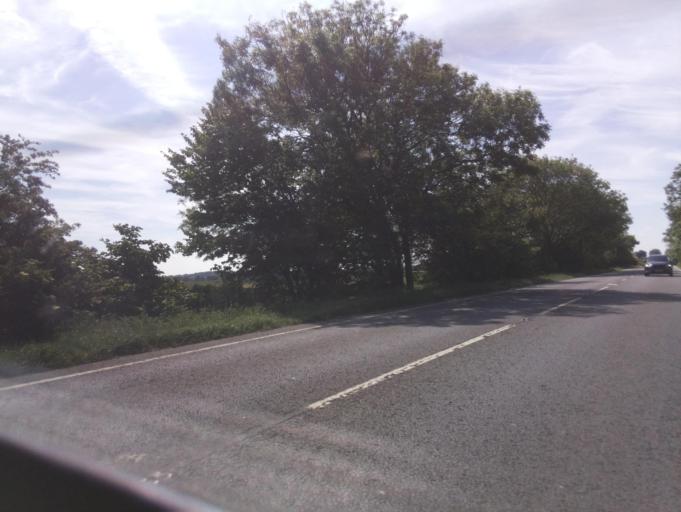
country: GB
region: England
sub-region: Lincolnshire
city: Burton
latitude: 53.3464
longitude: -0.5445
